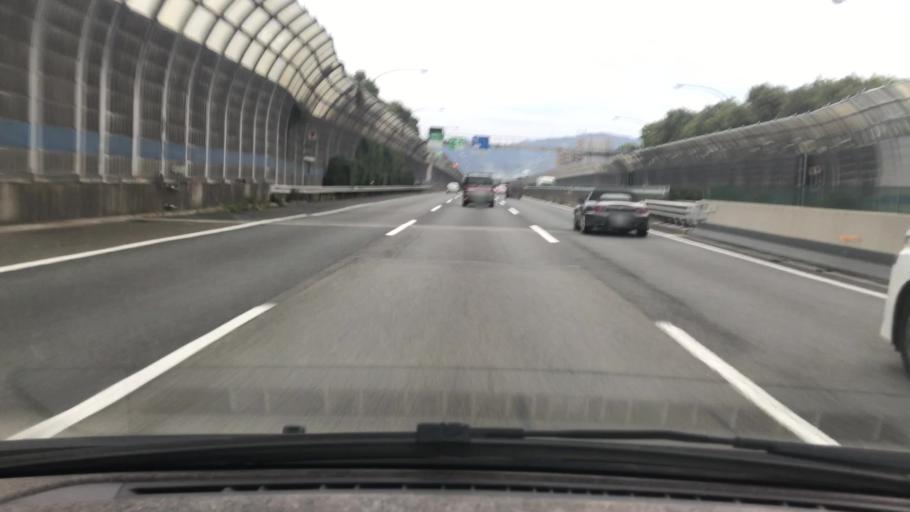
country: JP
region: Kyoto
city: Muko
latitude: 34.9490
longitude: 135.7326
